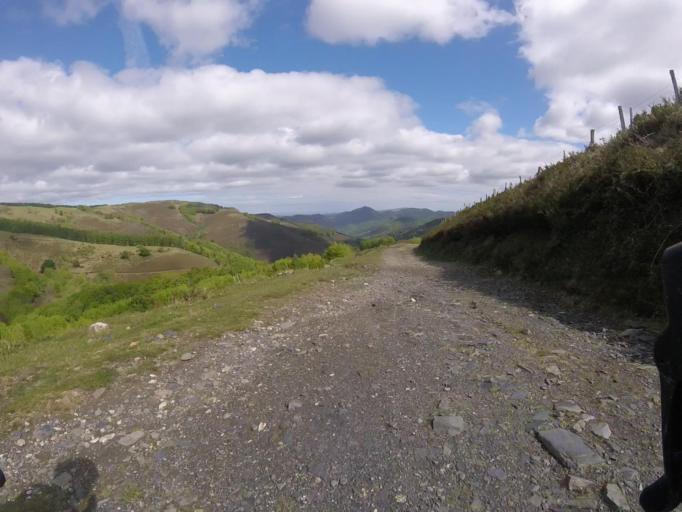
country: ES
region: Navarre
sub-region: Provincia de Navarra
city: Arano
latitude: 43.1750
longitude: -1.9083
